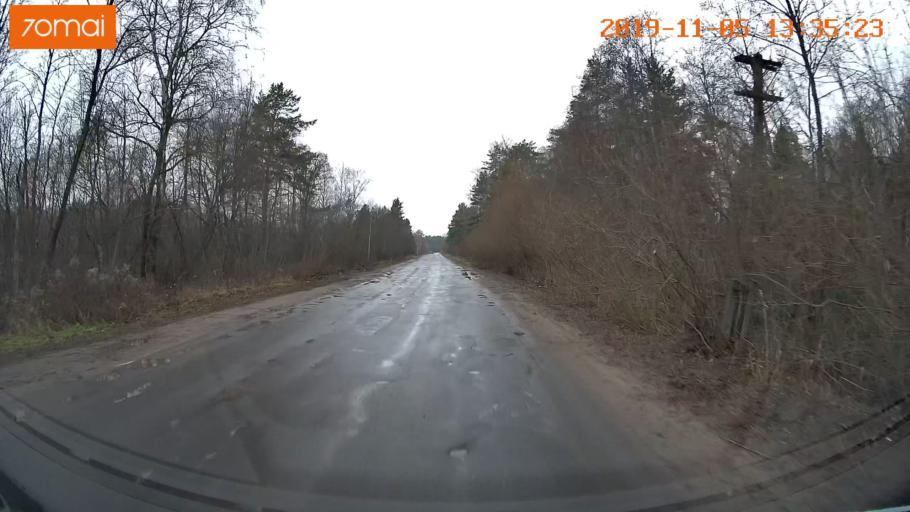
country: RU
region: Ivanovo
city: Shuya
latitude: 56.9075
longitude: 41.3877
